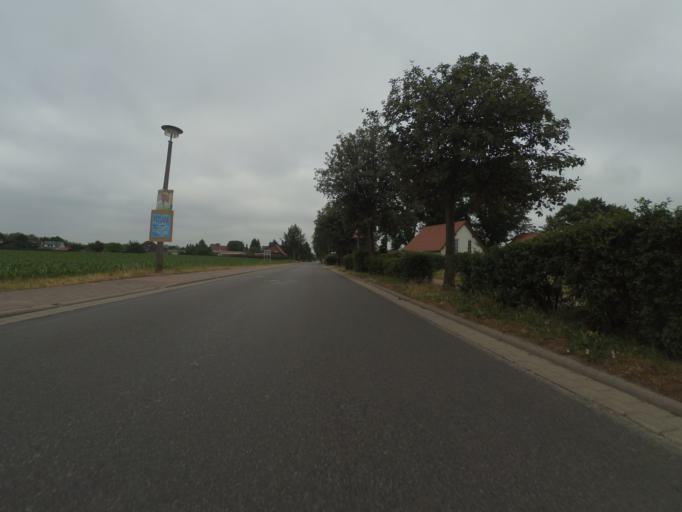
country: DE
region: Mecklenburg-Vorpommern
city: Plau am See
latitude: 53.4678
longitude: 12.2744
